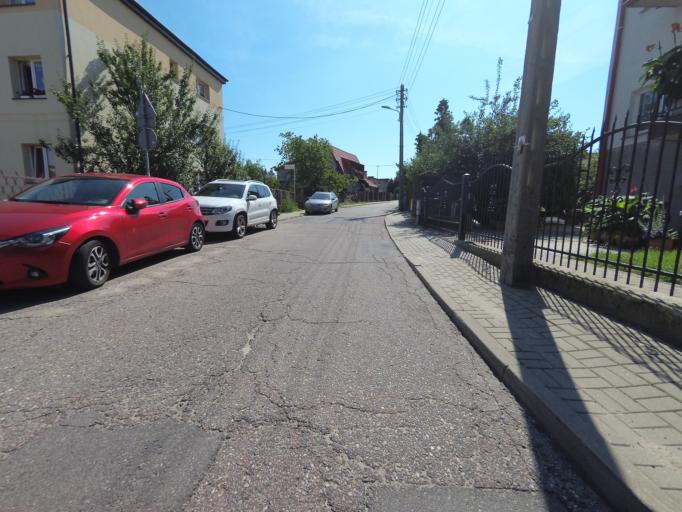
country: PL
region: Pomeranian Voivodeship
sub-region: Gdynia
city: Gdynia
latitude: 54.4939
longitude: 18.5151
